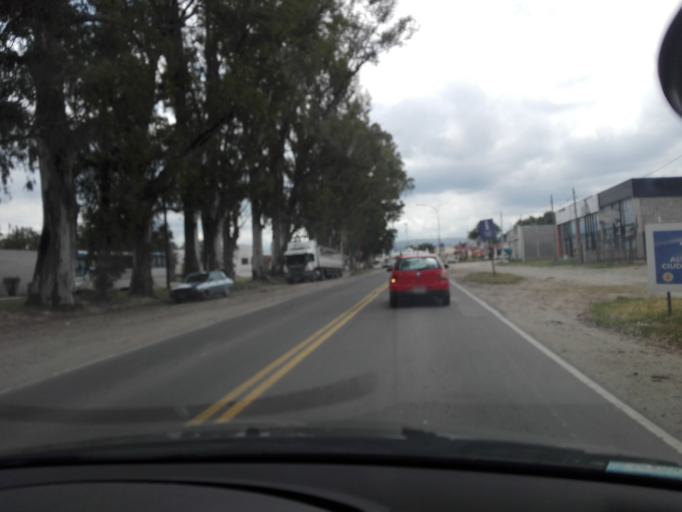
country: AR
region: Cordoba
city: Alta Gracia
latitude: -31.6583
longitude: -64.4071
